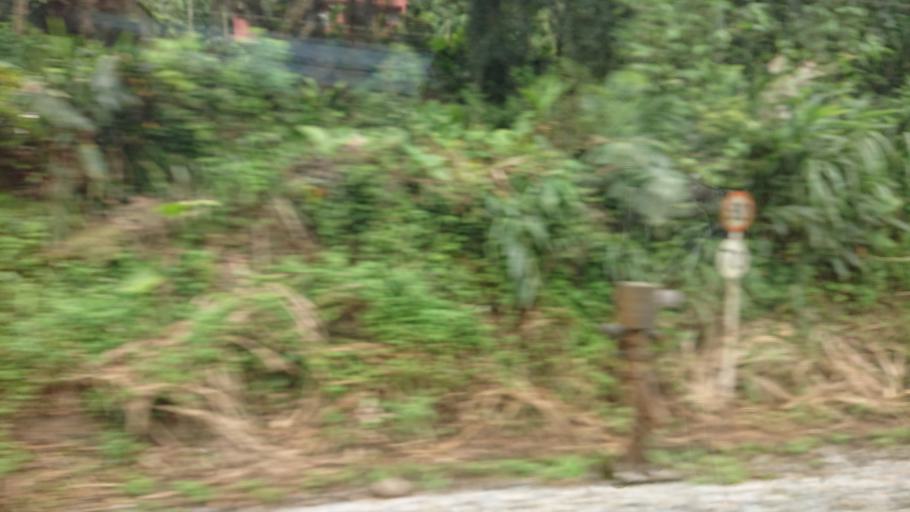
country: TW
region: Taiwan
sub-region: Keelung
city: Keelung
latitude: 25.0954
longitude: 121.8320
